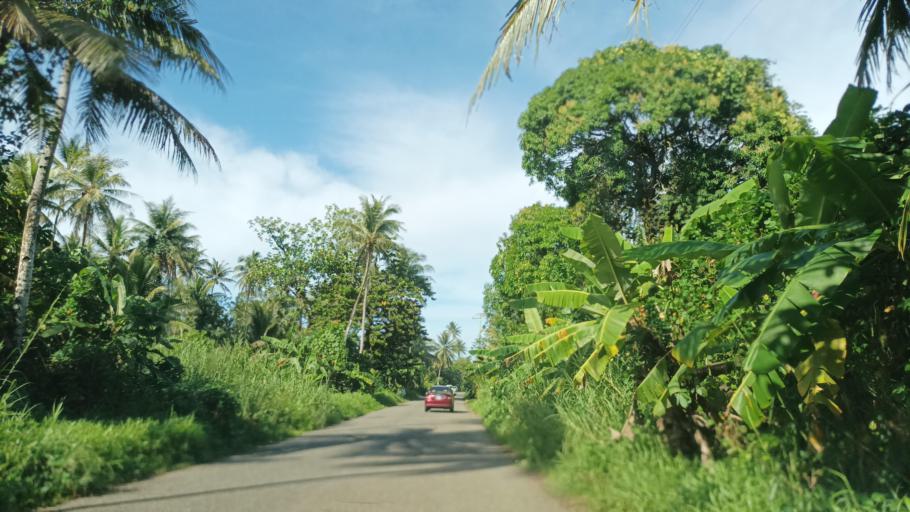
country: FM
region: Kosrae
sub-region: Lelu Municipality
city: Tofol
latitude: 5.3171
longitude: 163.0199
